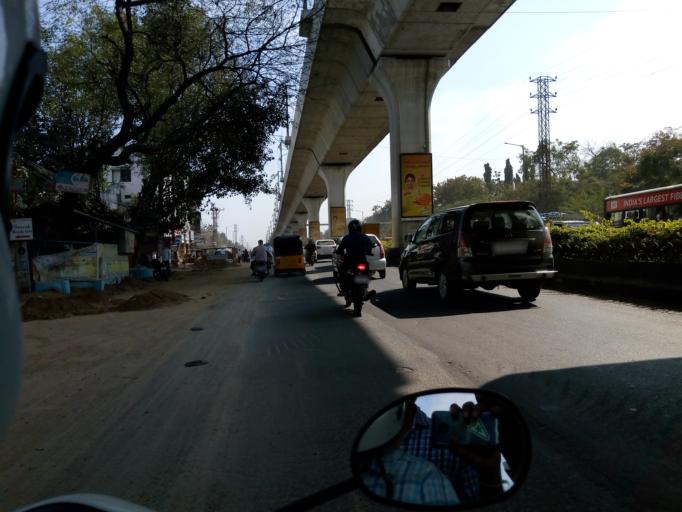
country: IN
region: Telangana
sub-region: Rangareddi
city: Uppal Kalan
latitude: 17.4071
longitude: 78.5545
